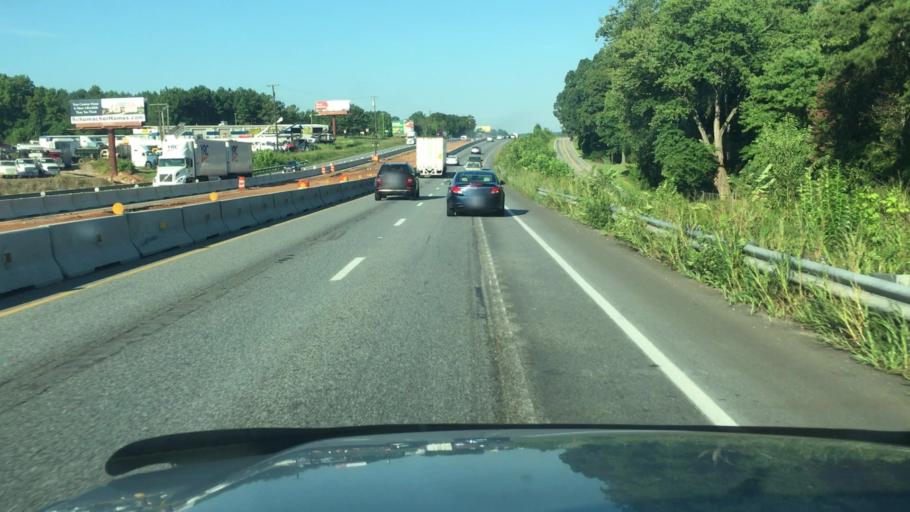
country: US
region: South Carolina
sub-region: Spartanburg County
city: Cowpens
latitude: 35.0379
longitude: -81.8320
